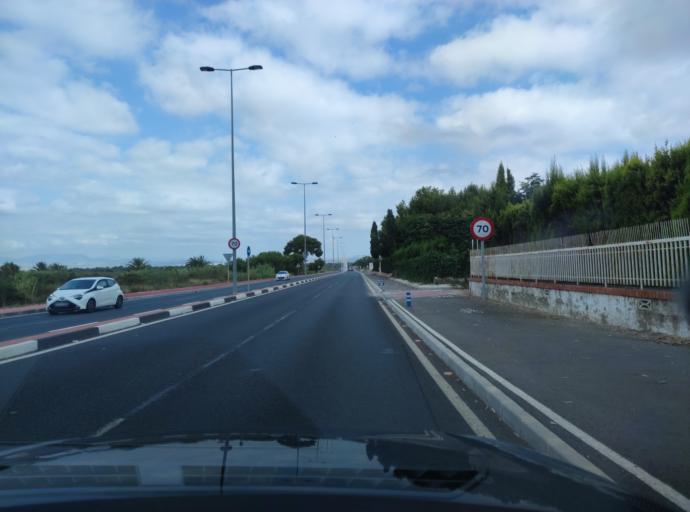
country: ES
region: Valencia
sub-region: Provincia de Alicante
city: Santa Pola
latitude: 38.2099
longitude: -0.5874
